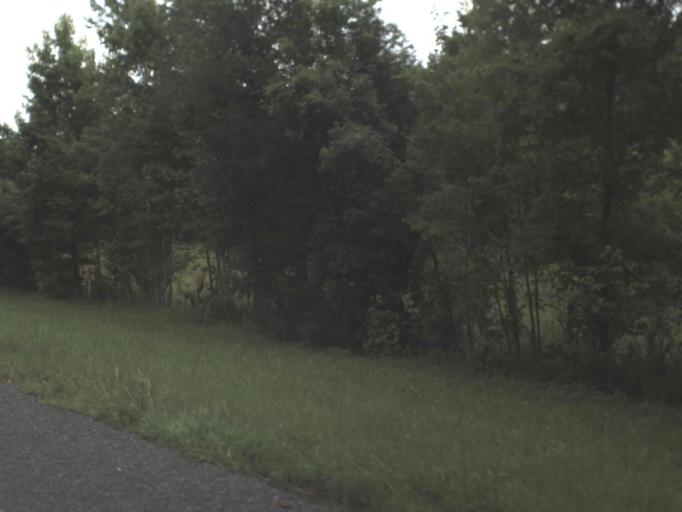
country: US
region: Florida
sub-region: Levy County
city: Bronson
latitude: 29.2853
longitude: -82.7427
